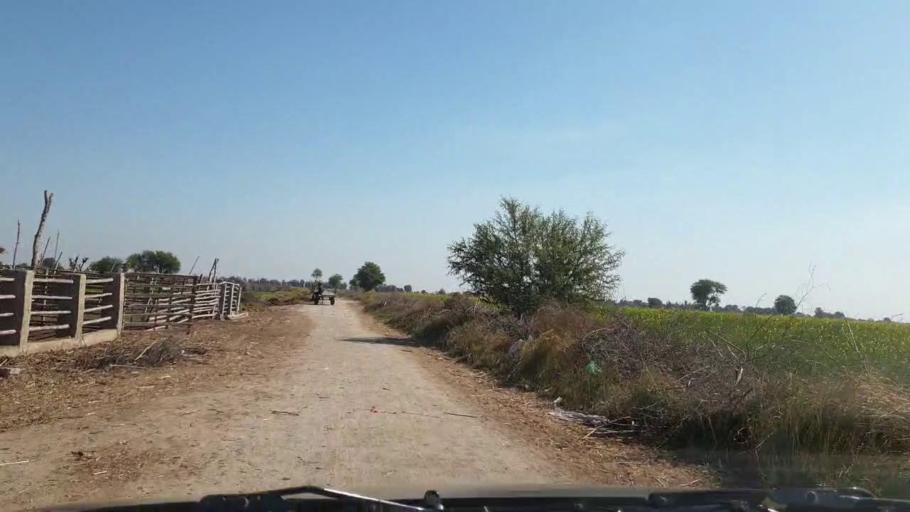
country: PK
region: Sindh
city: Sinjhoro
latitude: 26.1333
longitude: 68.8400
